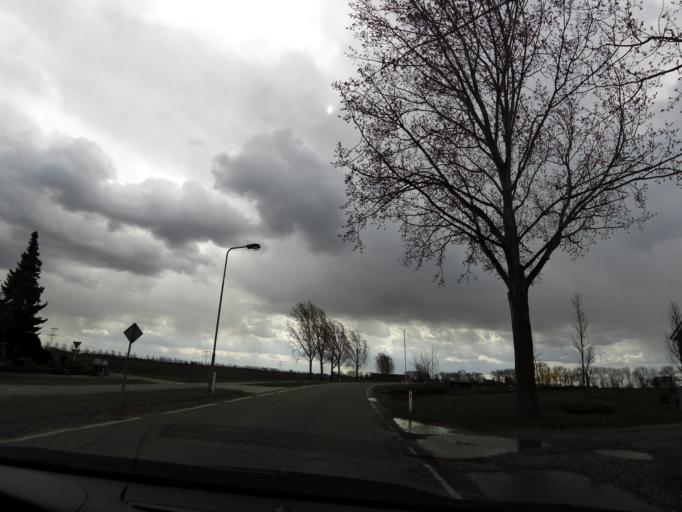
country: BE
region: Flanders
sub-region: Provincie Limburg
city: Maaseik
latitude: 51.0793
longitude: 5.8119
